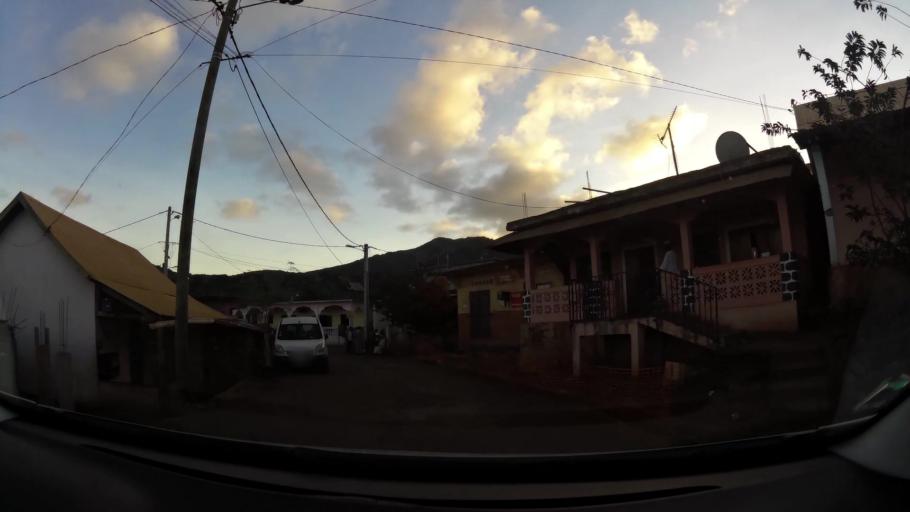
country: YT
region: Dembeni
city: Dembeni
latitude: -12.8682
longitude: 45.1952
